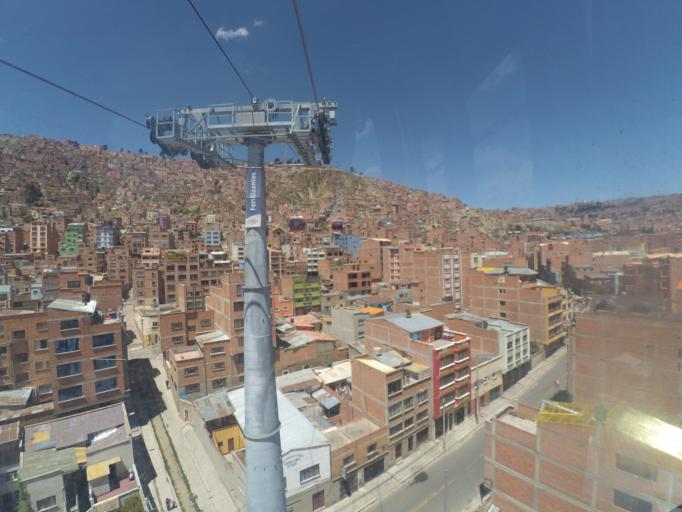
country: BO
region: La Paz
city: La Paz
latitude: -16.4978
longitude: -68.1571
